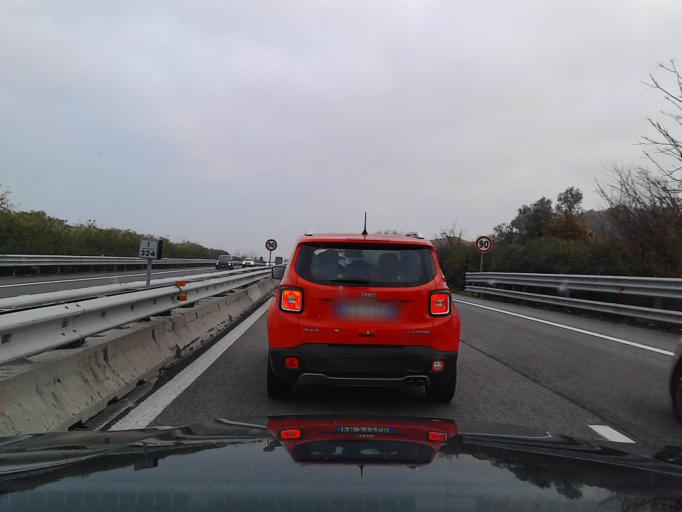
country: IT
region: Abruzzo
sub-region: Provincia di Teramo
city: Tortoreto Lido
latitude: 42.7967
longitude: 13.9308
